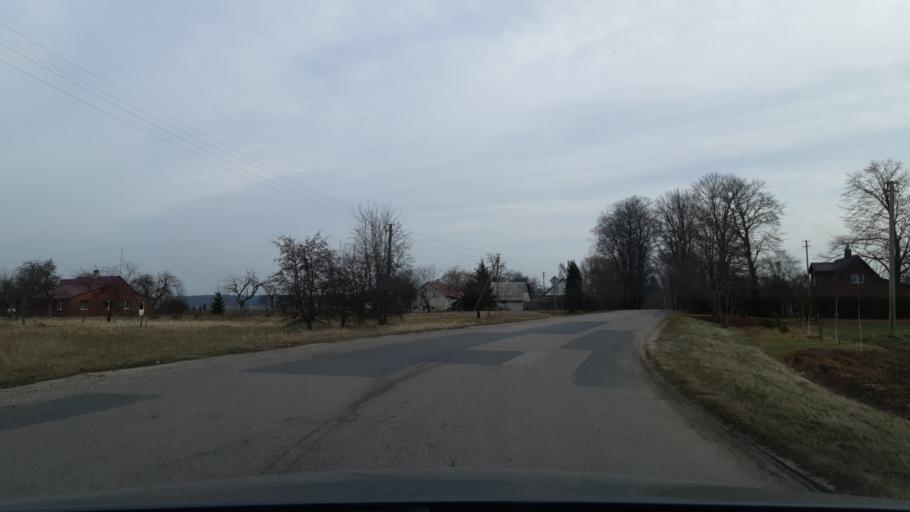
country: LT
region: Marijampoles apskritis
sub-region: Marijampole Municipality
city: Marijampole
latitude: 54.7183
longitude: 23.3234
